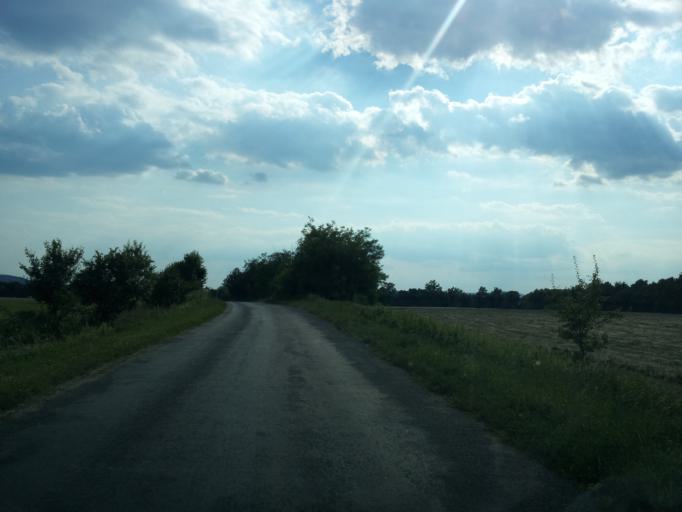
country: HU
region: Veszprem
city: Zanka
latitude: 46.9651
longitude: 17.6490
